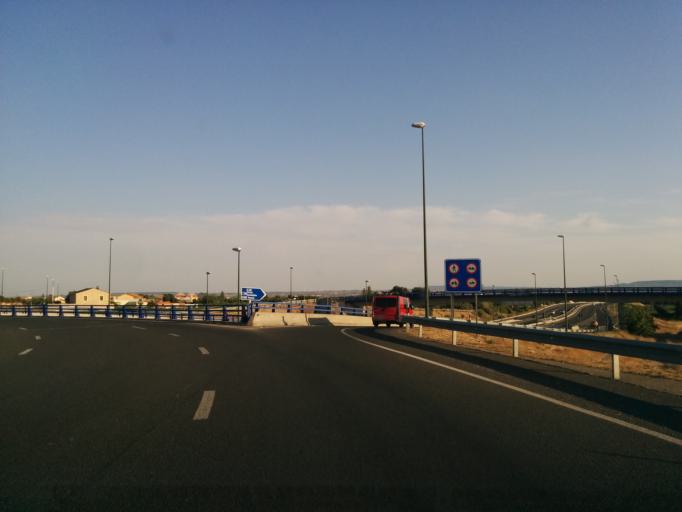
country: ES
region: Aragon
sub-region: Provincia de Zaragoza
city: Zaragoza
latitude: 41.6655
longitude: -0.8387
